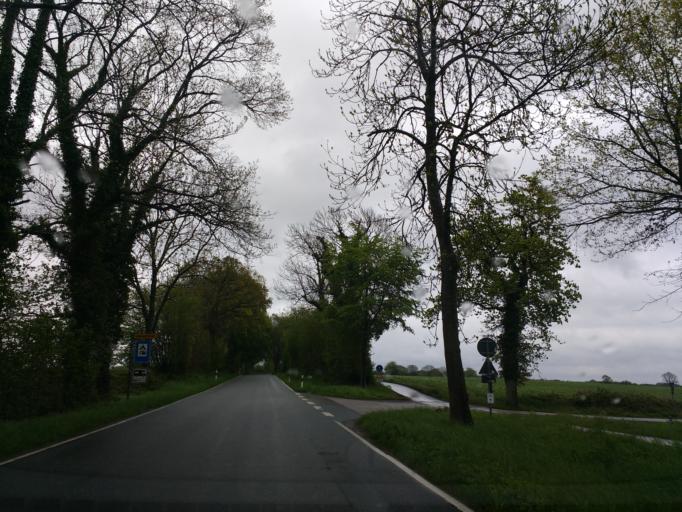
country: DE
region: Schleswig-Holstein
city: Waabs
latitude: 54.5221
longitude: 9.9611
